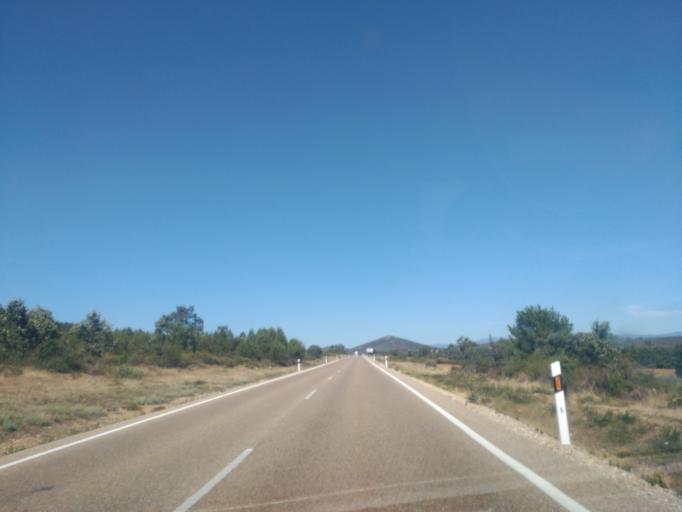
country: ES
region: Castille and Leon
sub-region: Provincia de Zamora
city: Otero de Bodas
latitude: 41.9282
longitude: -6.1098
